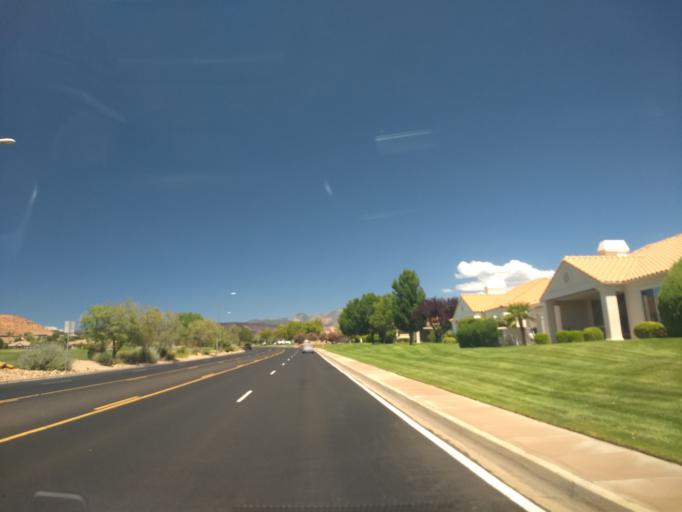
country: US
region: Utah
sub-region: Washington County
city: Washington
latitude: 37.1374
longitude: -113.5263
